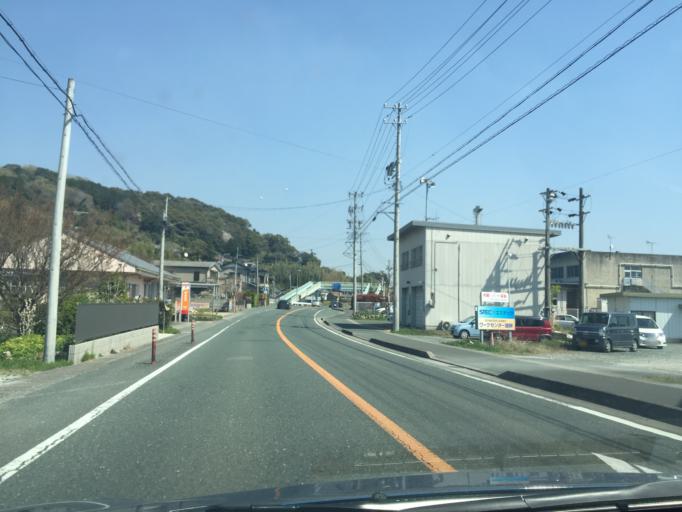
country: JP
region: Shizuoka
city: Kosai-shi
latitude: 34.8020
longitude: 137.6226
